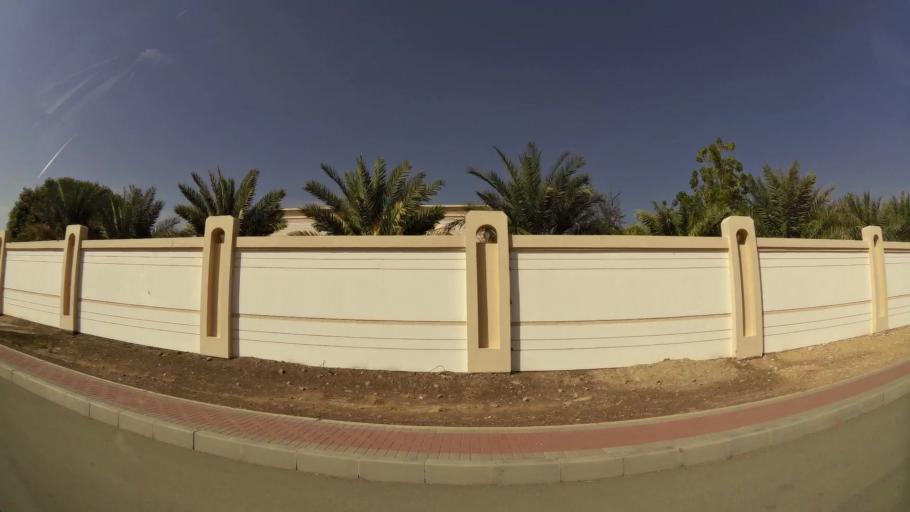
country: AE
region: Abu Dhabi
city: Al Ain
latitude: 24.0865
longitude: 55.9324
